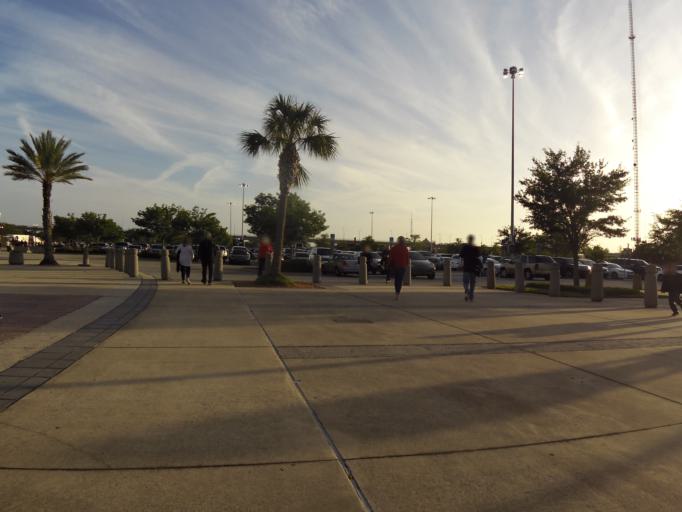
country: US
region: Florida
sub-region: Duval County
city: Jacksonville
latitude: 30.3244
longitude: -81.6391
